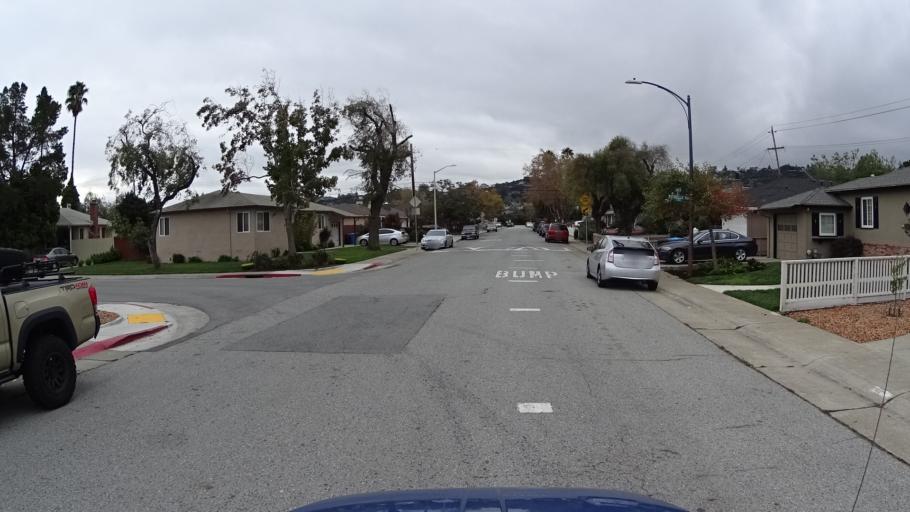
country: US
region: California
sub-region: San Mateo County
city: Belmont
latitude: 37.5366
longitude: -122.2888
